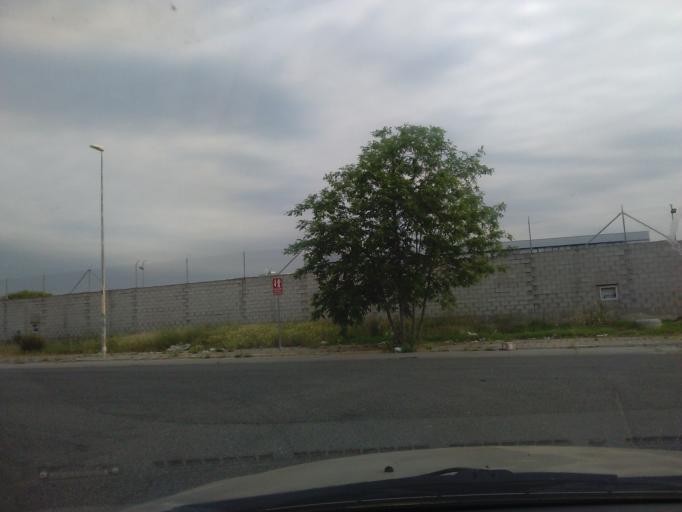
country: ES
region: Andalusia
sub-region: Provincia de Sevilla
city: Sevilla
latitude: 37.3801
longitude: -5.9276
